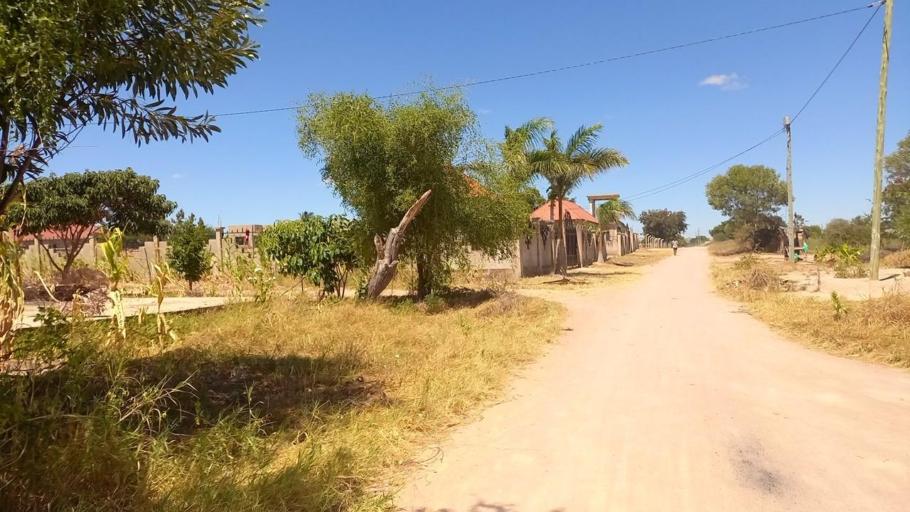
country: TZ
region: Dodoma
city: Dodoma
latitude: -6.1185
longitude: 35.7395
